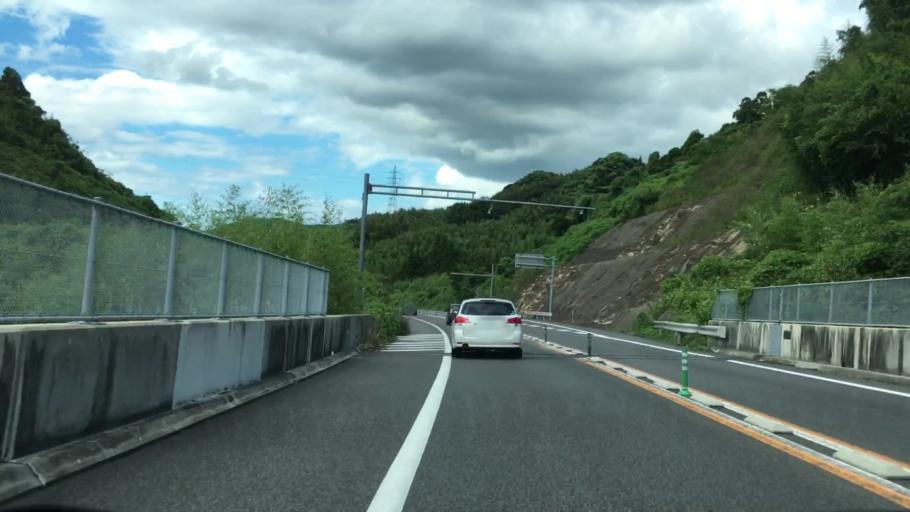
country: JP
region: Saga Prefecture
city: Karatsu
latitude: 33.4308
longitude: 130.0481
